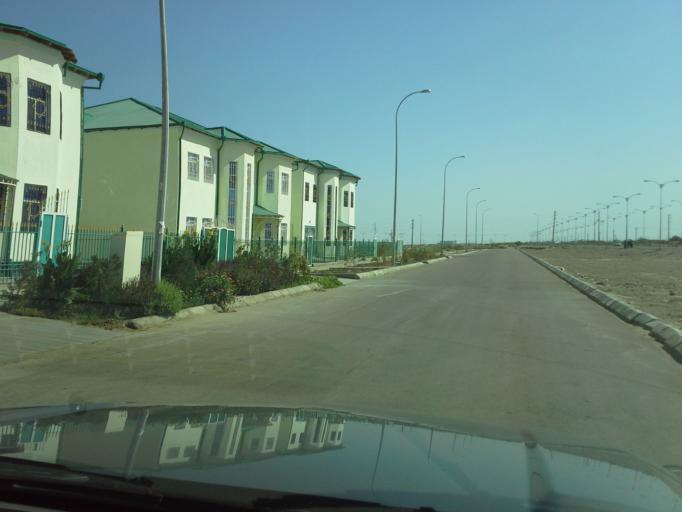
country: TM
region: Dasoguz
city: Dasoguz
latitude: 41.8060
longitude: 59.9524
